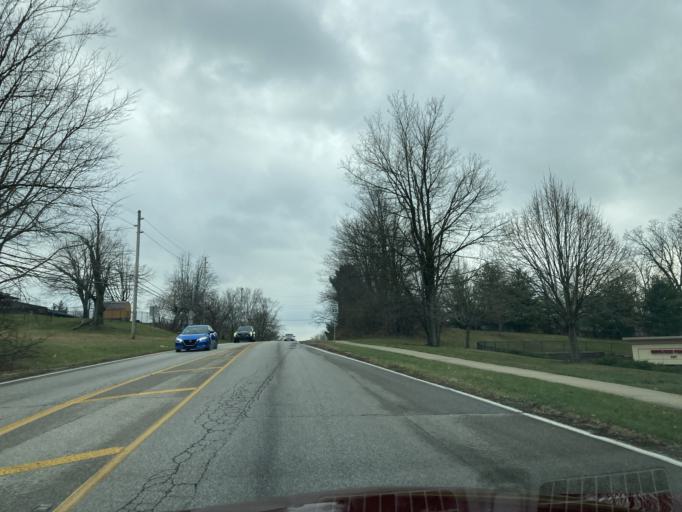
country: US
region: Indiana
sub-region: Monroe County
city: Bloomington
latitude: 39.1343
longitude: -86.5315
